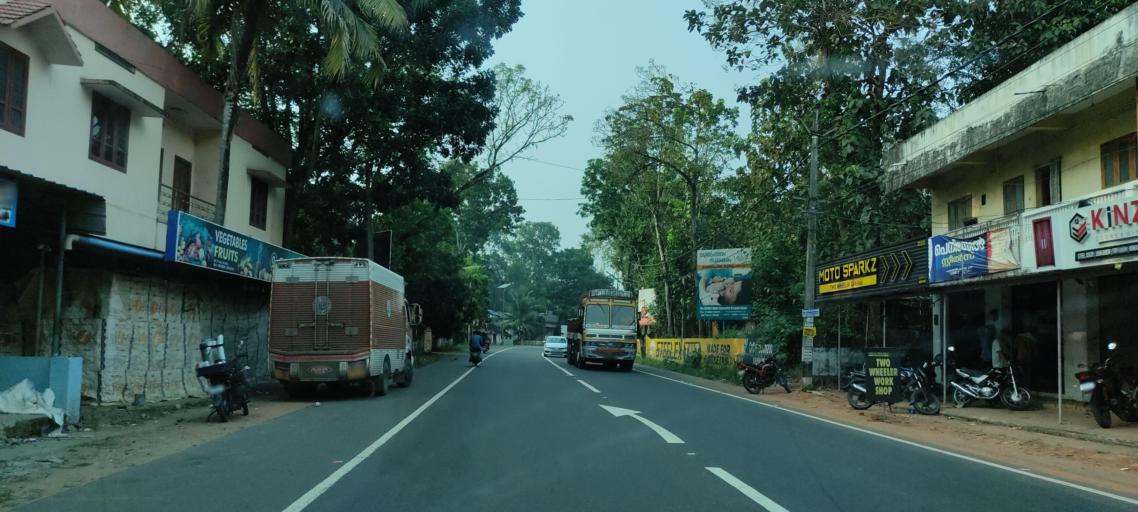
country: IN
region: Kerala
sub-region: Pattanamtitta
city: Adur
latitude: 9.1003
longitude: 76.7509
